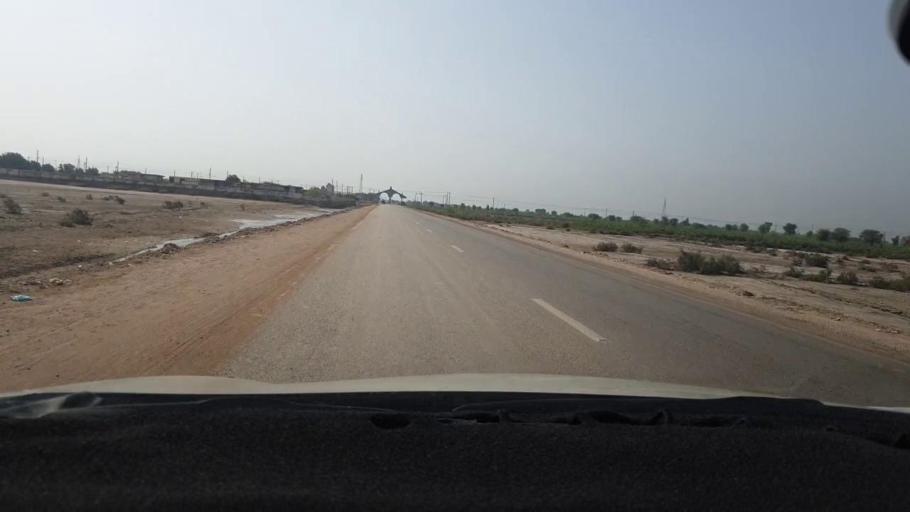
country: PK
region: Sindh
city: Sanghar
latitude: 26.0319
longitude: 68.9527
